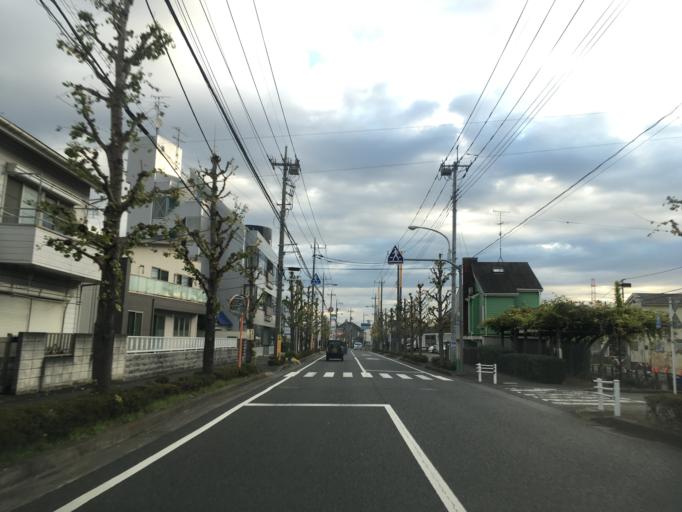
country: JP
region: Tokyo
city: Kokubunji
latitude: 35.6500
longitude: 139.4910
